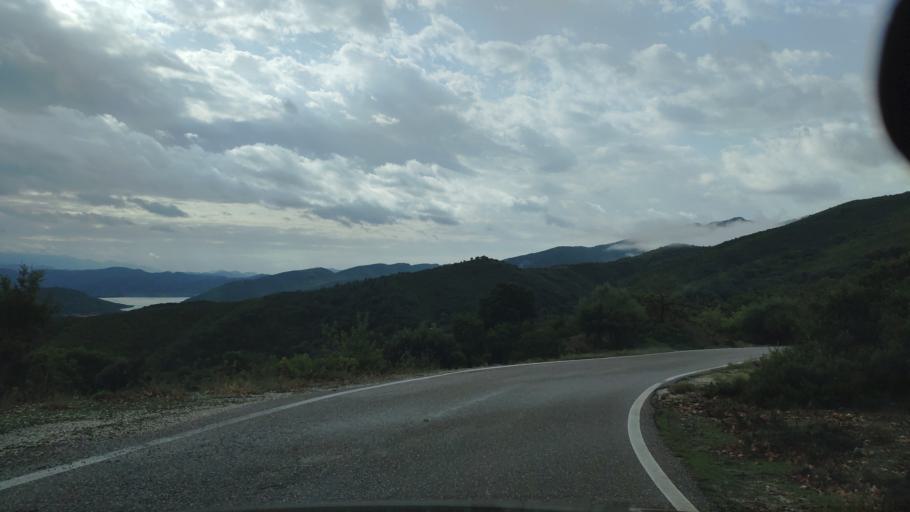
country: GR
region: West Greece
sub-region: Nomos Aitolias kai Akarnanias
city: Sardinia
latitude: 38.8470
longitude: 21.3202
